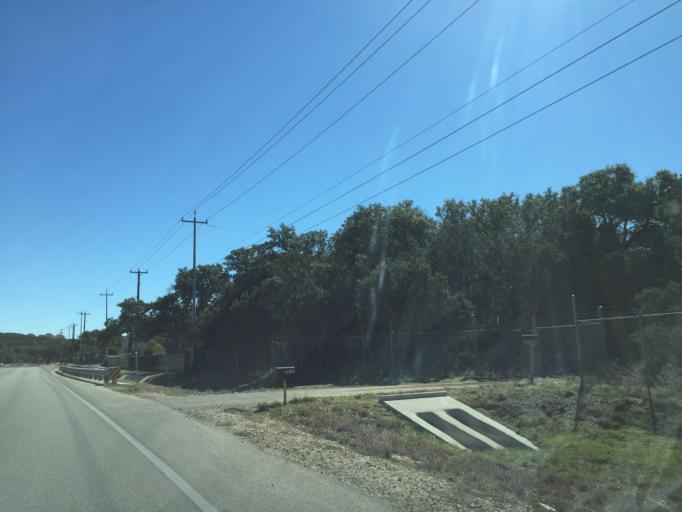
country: US
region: Texas
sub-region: Bexar County
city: Timberwood Park
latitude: 29.6891
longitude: -98.4472
